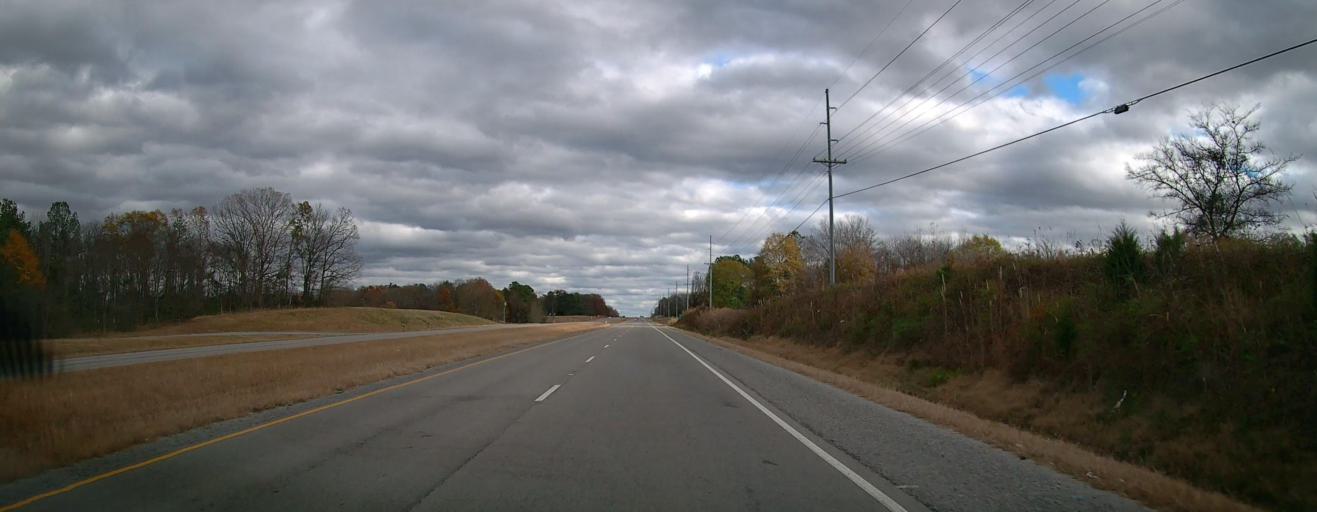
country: US
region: Alabama
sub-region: Lawrence County
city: Town Creek
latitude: 34.5719
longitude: -87.3903
